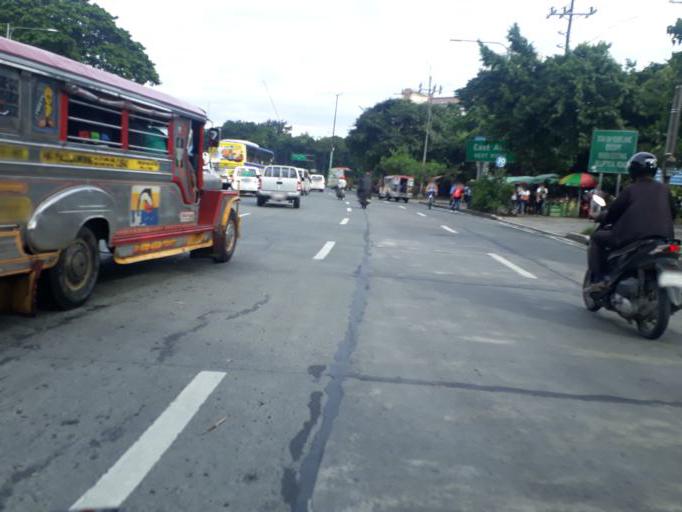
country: PH
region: Metro Manila
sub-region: Quezon City
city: Quezon City
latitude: 14.6494
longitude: 121.0475
